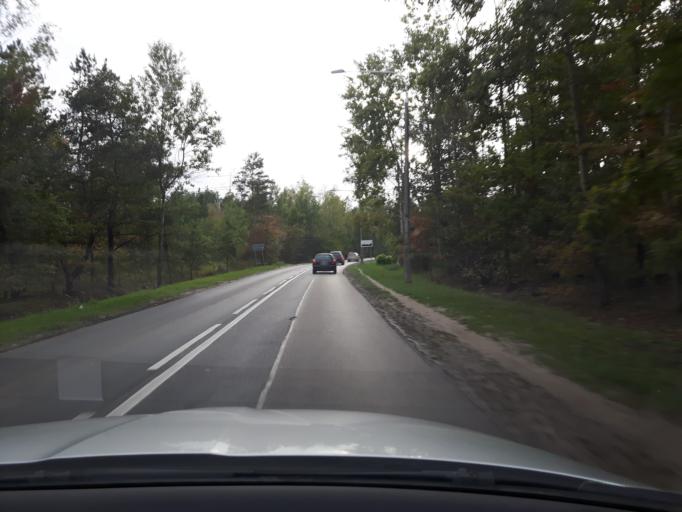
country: PL
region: Masovian Voivodeship
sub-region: Powiat wolominski
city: Zabki
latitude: 52.2926
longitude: 21.1332
